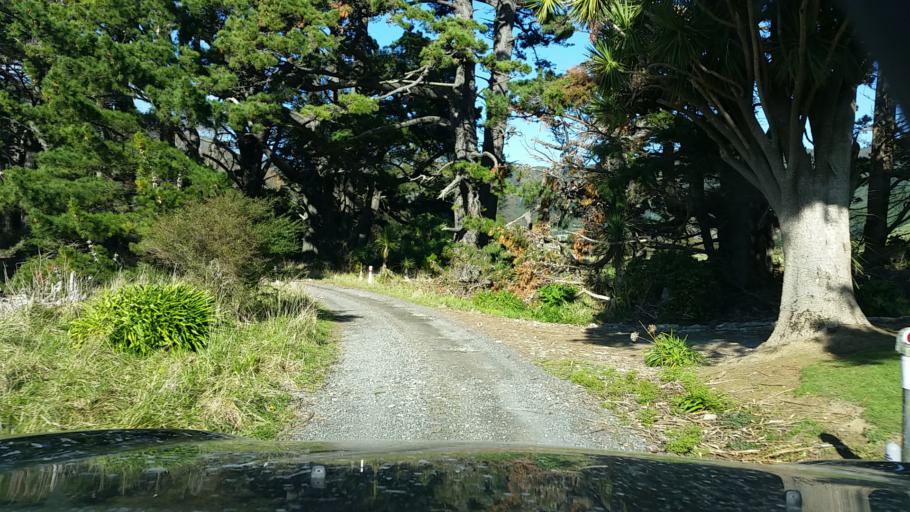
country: NZ
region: Marlborough
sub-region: Marlborough District
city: Picton
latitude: -41.1131
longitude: 174.0348
